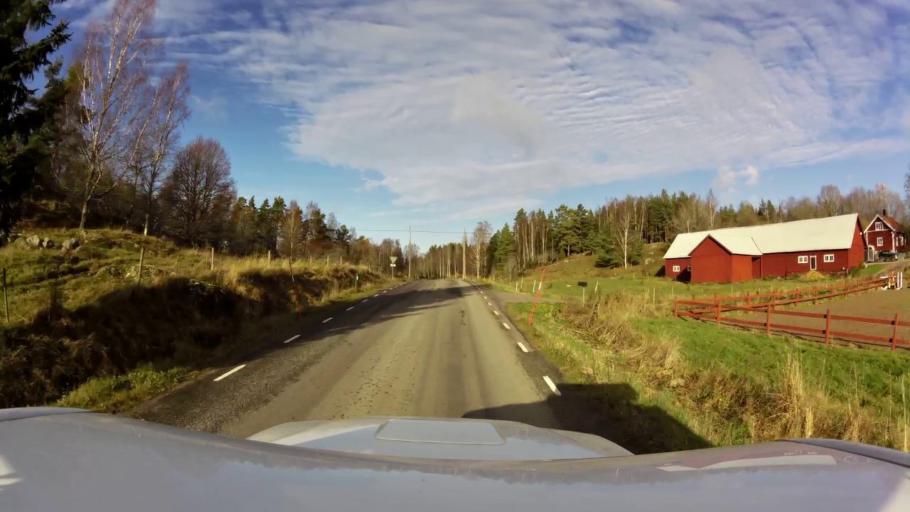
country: SE
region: OEstergoetland
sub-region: Linkopings Kommun
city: Sturefors
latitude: 58.3143
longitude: 15.6706
